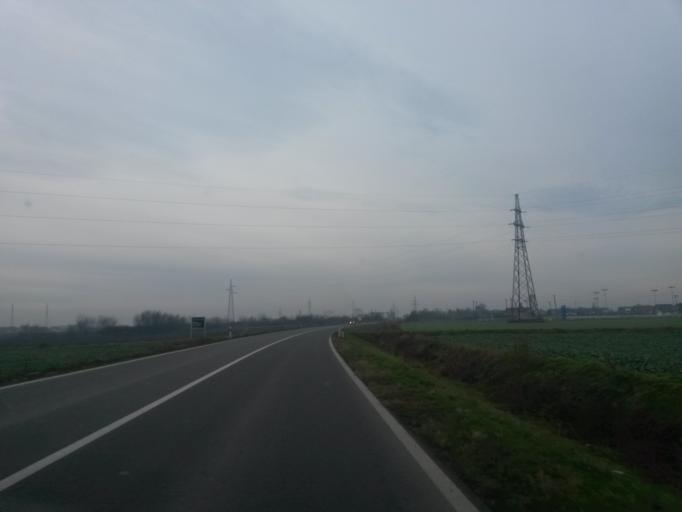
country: HR
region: Osjecko-Baranjska
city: Brijest
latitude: 45.5188
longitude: 18.6819
